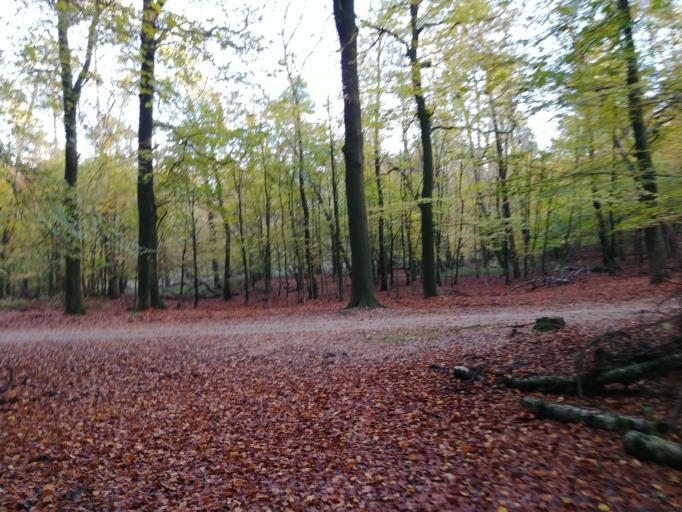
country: NL
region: Gelderland
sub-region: Gemeente Rheden
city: Rheden
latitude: 52.0445
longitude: 6.0297
